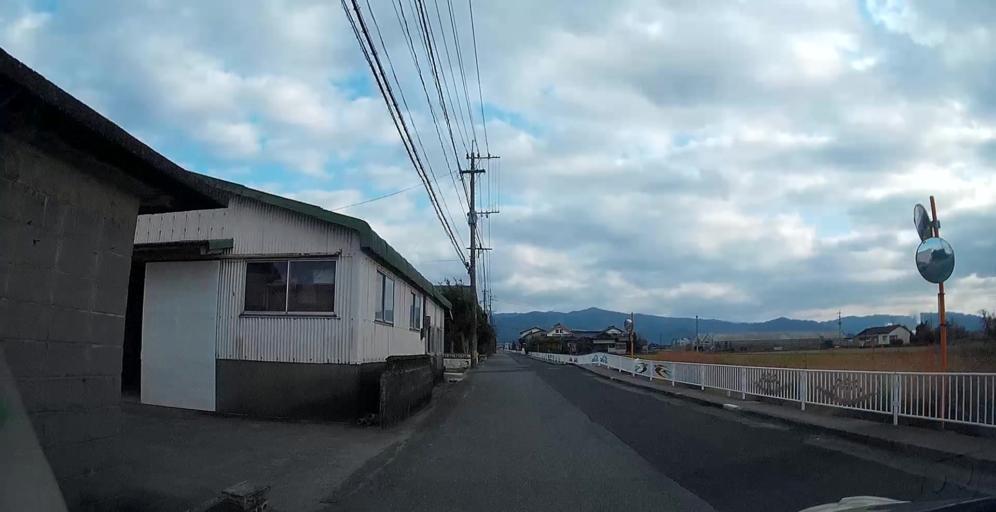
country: JP
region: Kumamoto
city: Yatsushiro
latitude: 32.5471
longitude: 130.6166
